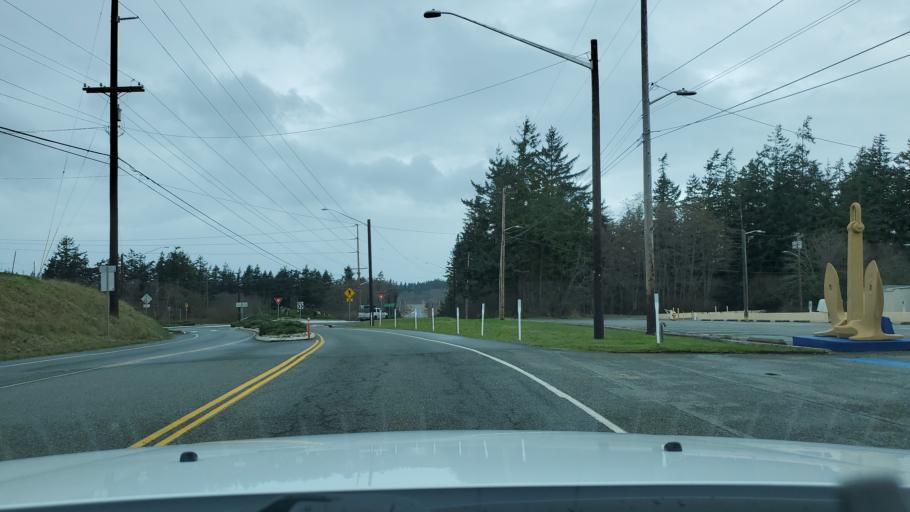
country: US
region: Washington
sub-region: Island County
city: Ault Field
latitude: 48.3259
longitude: -122.6730
